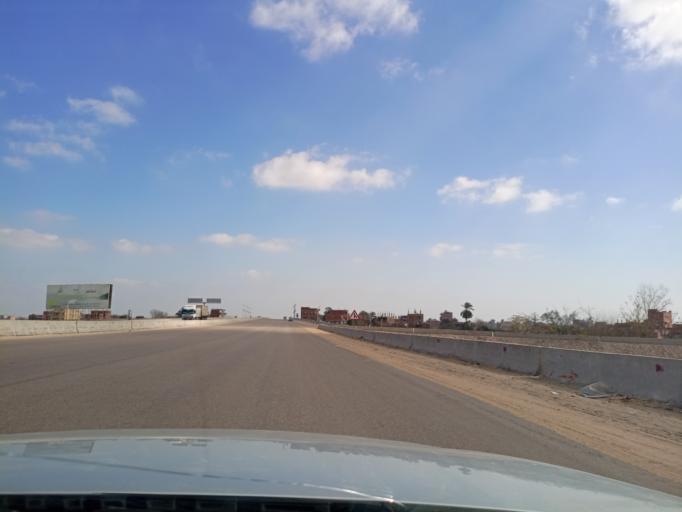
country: EG
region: Muhafazat al Minufiyah
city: Al Bajur
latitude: 30.4037
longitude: 31.0355
